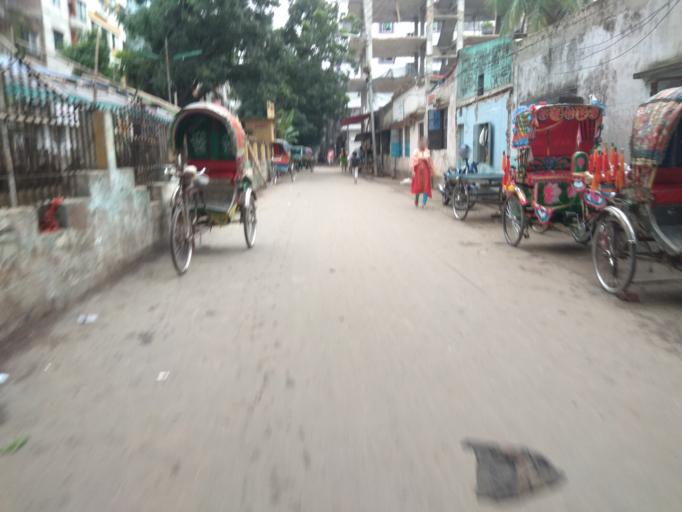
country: BD
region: Dhaka
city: Tungi
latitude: 23.8256
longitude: 90.3761
